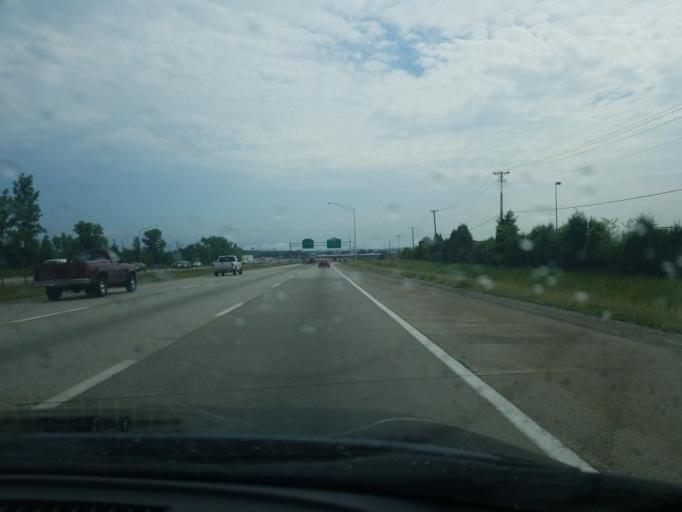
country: US
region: Kentucky
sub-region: Bullitt County
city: Shepherdsville
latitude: 38.0025
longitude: -85.7026
